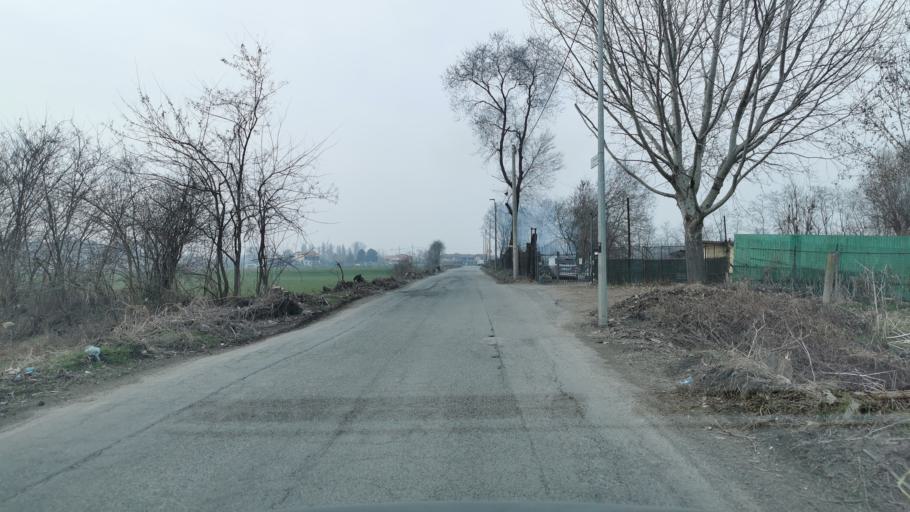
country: IT
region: Piedmont
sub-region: Provincia di Torino
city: Turin
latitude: 45.1188
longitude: 7.6928
